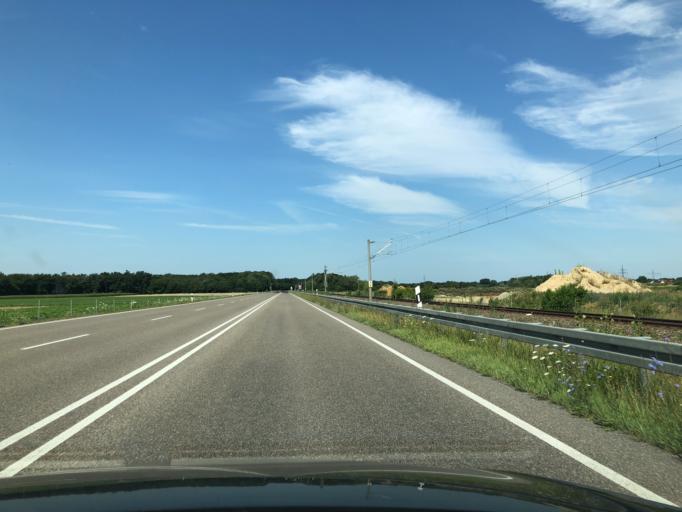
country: DE
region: Bavaria
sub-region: Upper Bavaria
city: Karlskron
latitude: 48.7061
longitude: 11.3836
